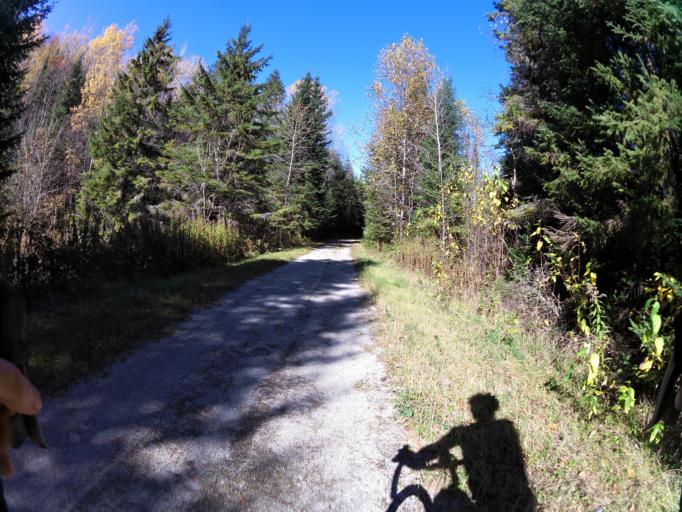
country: CA
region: Quebec
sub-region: Outaouais
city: Wakefield
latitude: 45.8532
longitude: -75.9919
